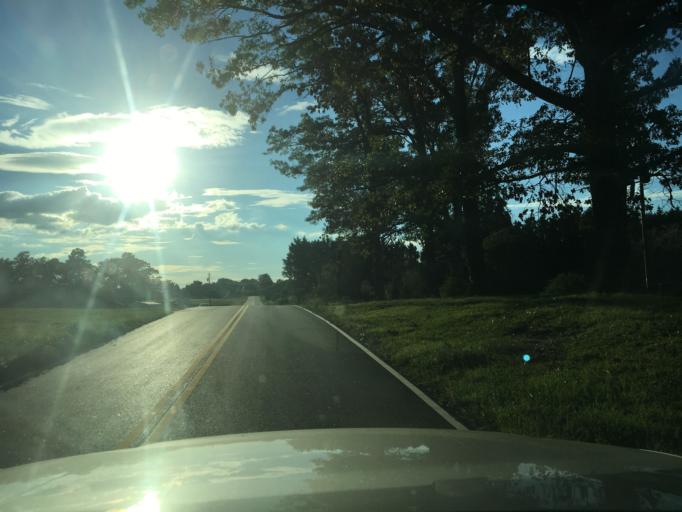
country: US
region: South Carolina
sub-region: Spartanburg County
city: Roebuck
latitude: 34.9013
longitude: -82.0018
